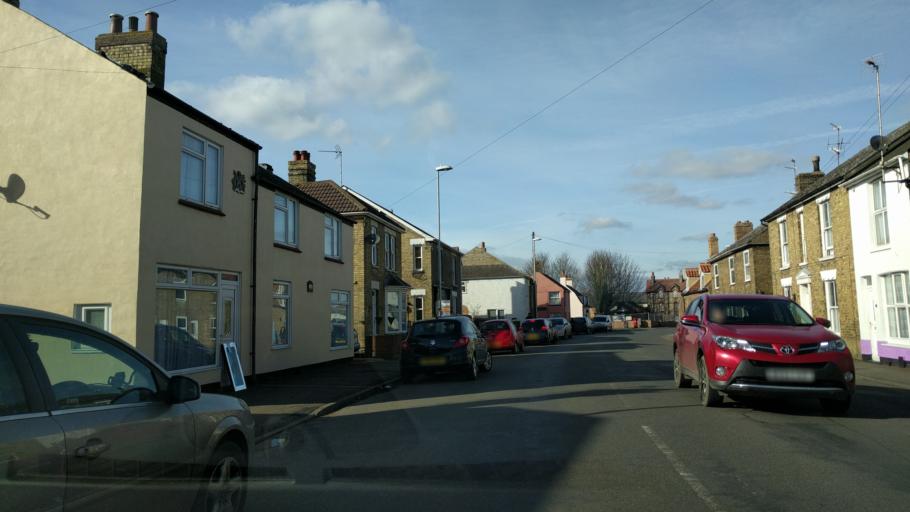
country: GB
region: England
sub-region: Cambridgeshire
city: Chatteris
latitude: 52.4596
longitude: 0.0453
